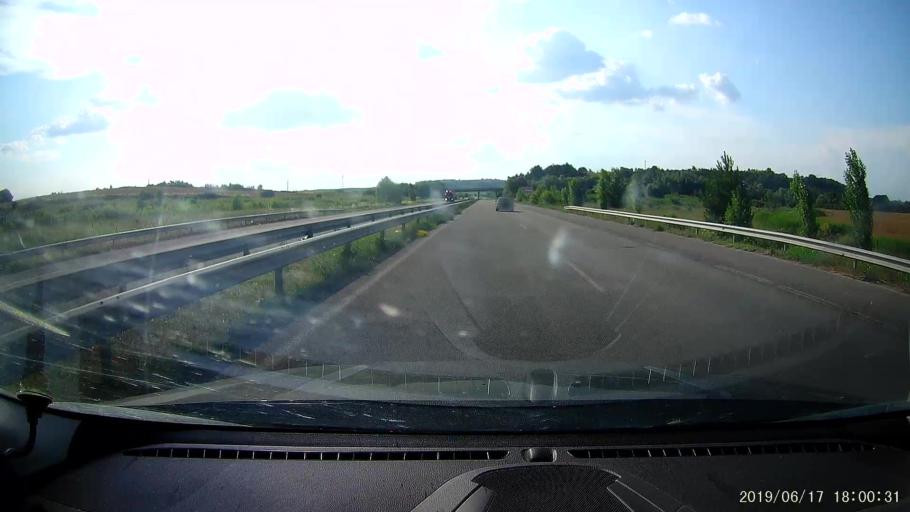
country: BG
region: Khaskovo
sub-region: Obshtina Svilengrad
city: Svilengrad
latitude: 41.7375
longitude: 26.2776
